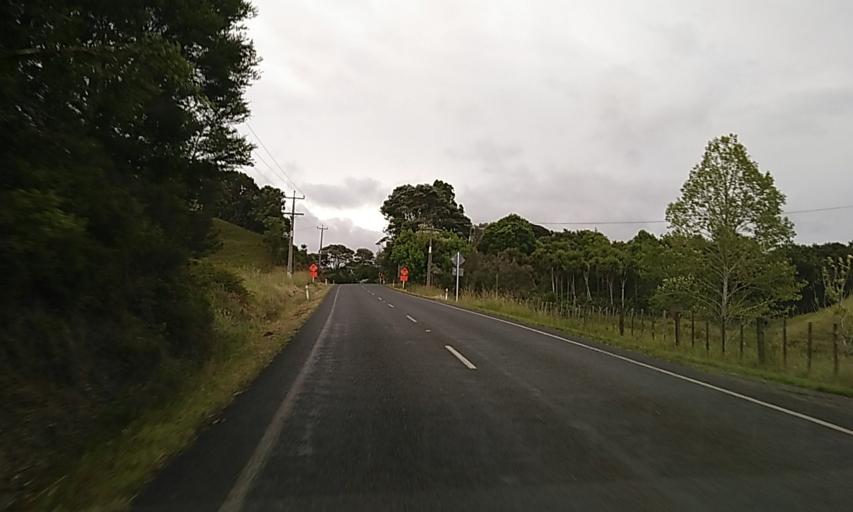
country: NZ
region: Auckland
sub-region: Auckland
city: Pukekohe East
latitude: -37.2989
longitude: 174.9376
